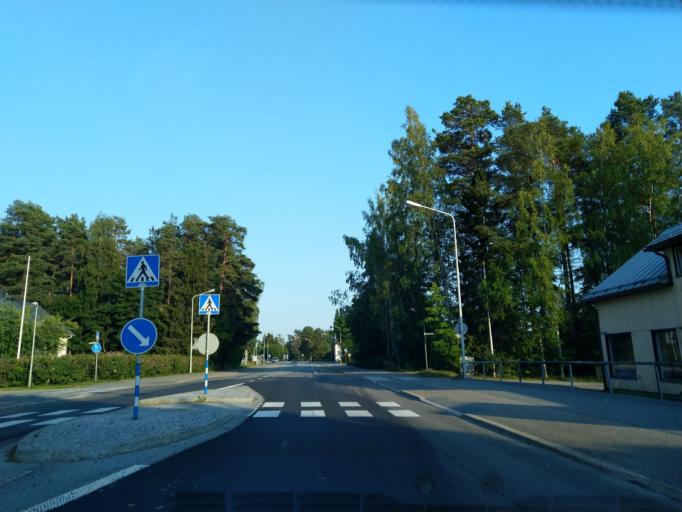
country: FI
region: Satakunta
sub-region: Pohjois-Satakunta
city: Kankaanpaeae
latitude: 61.8093
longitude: 22.3835
